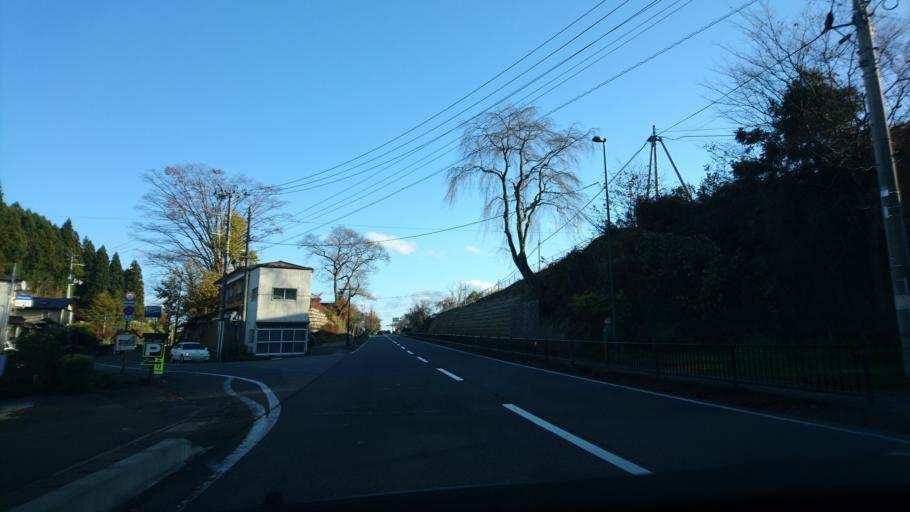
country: JP
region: Iwate
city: Ichinoseki
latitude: 38.9978
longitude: 141.1092
